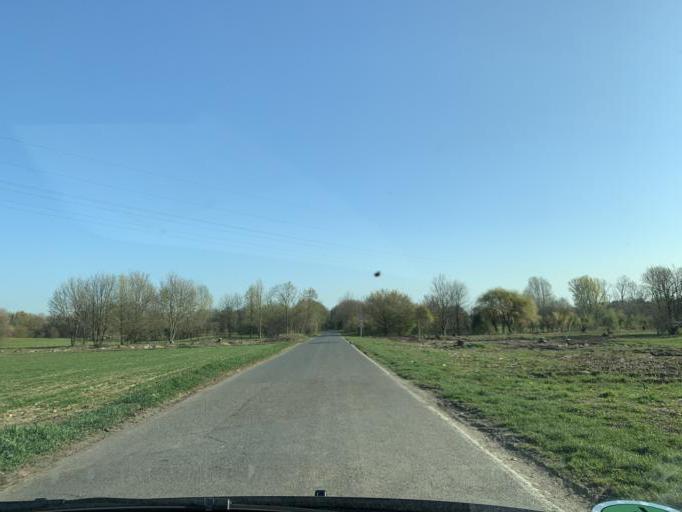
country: DE
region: North Rhine-Westphalia
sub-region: Regierungsbezirk Koln
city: Titz
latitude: 51.0886
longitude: 6.4032
